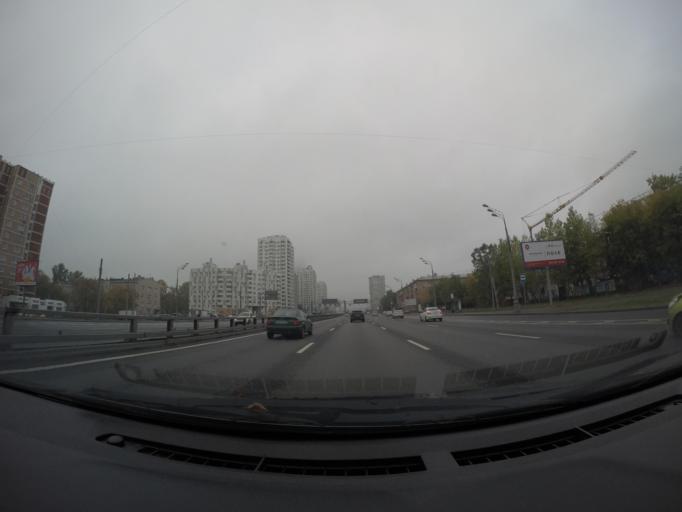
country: RU
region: Moskovskaya
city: Khoroshevo-Mnevniki
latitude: 55.7729
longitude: 37.4902
